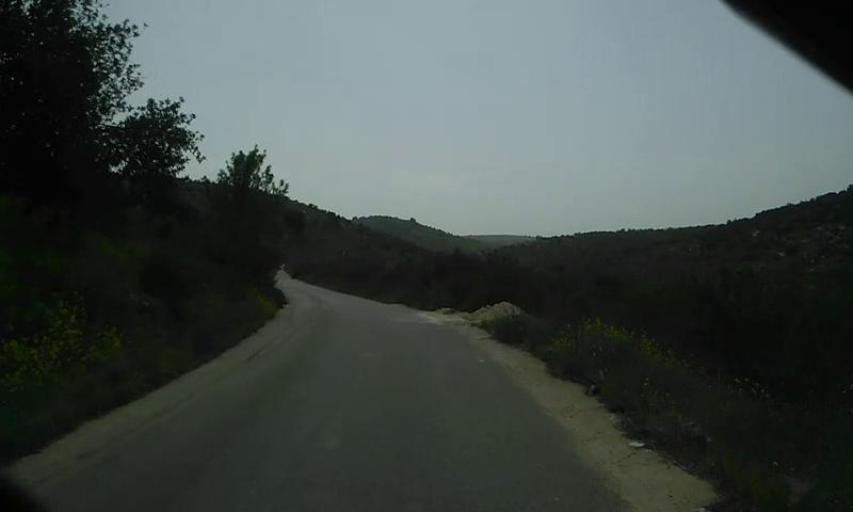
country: PS
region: West Bank
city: Silat al Harithiyah
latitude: 32.5147
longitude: 35.2149
